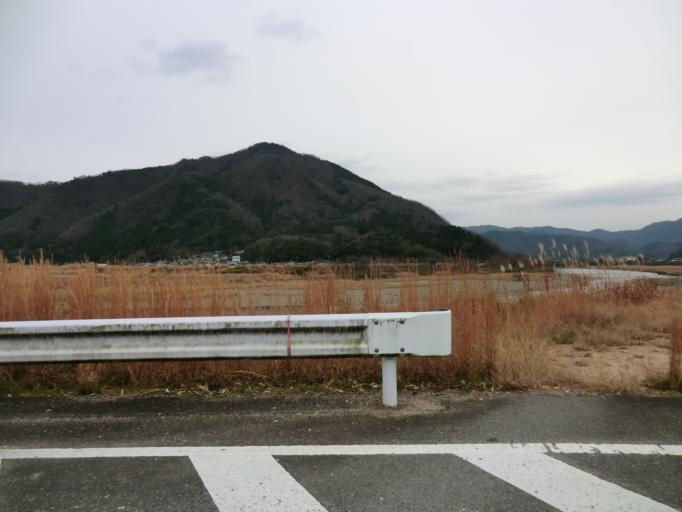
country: JP
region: Hyogo
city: Toyooka
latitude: 35.4478
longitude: 134.7714
